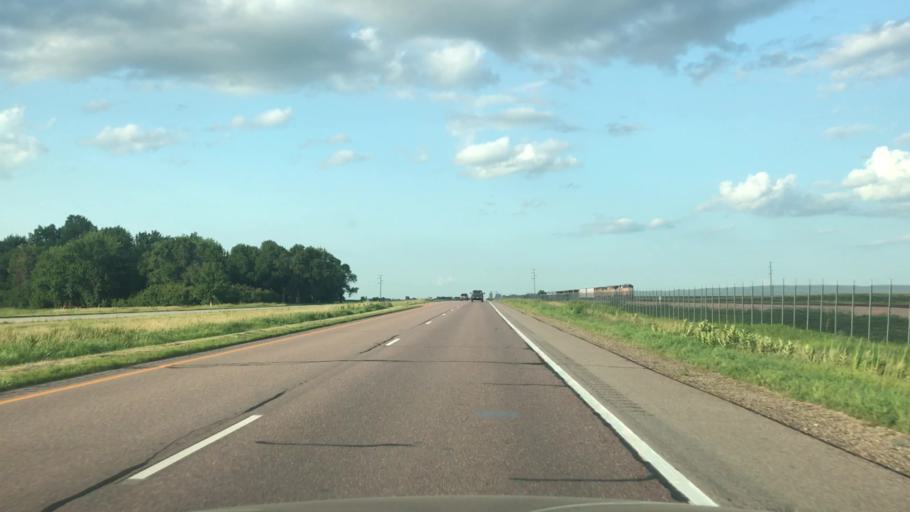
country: US
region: Minnesota
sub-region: Nobles County
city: Worthington
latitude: 43.6644
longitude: -95.5241
